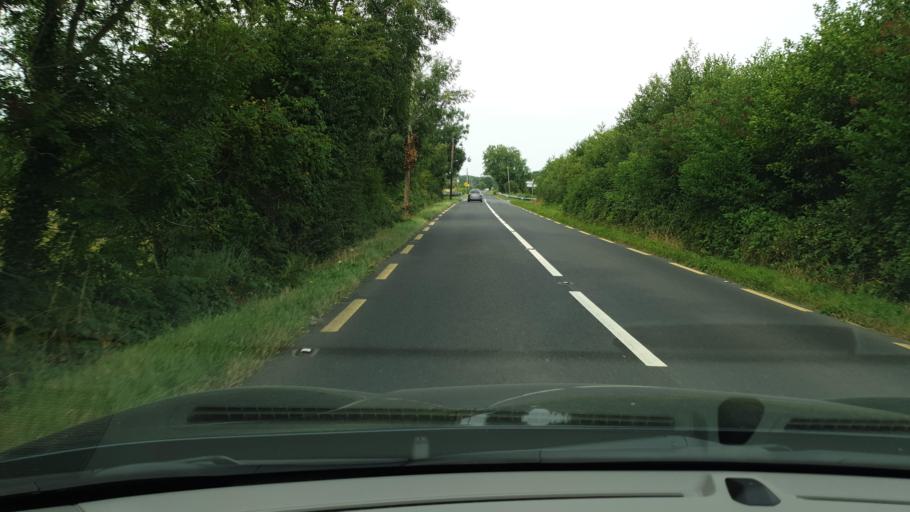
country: IE
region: Leinster
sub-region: An Mhi
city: Trim
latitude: 53.6332
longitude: -6.8094
